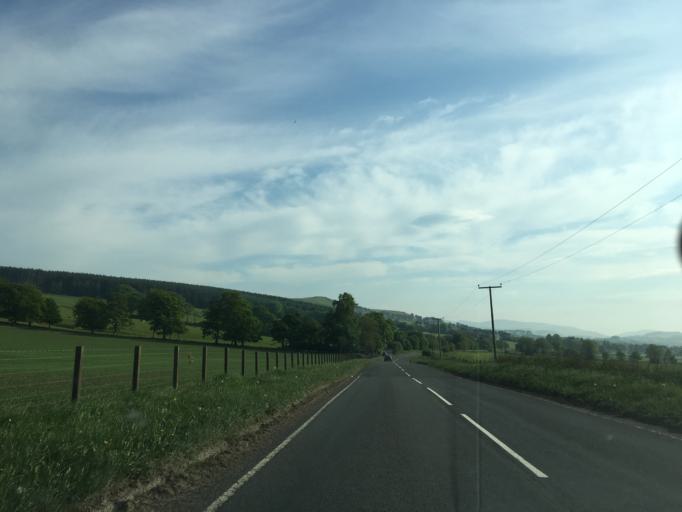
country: GB
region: Scotland
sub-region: The Scottish Borders
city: West Linton
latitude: 55.7428
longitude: -3.2959
